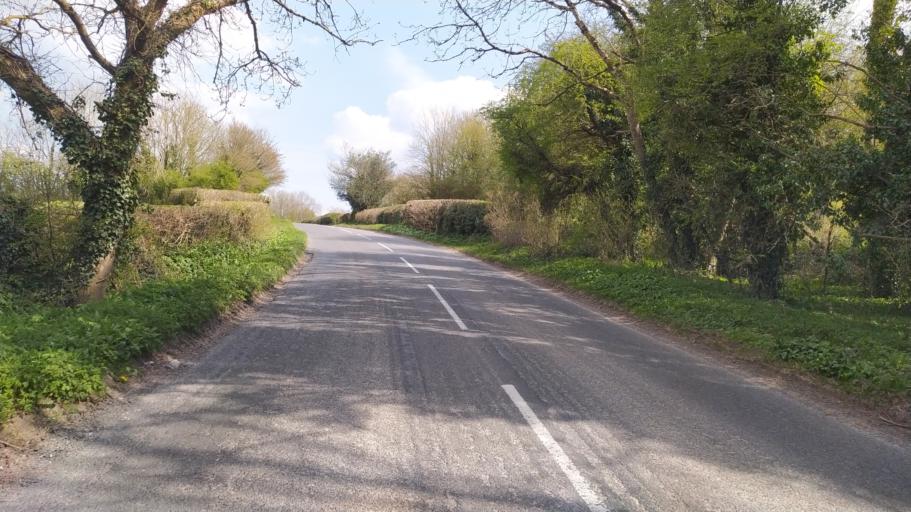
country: GB
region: England
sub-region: Somerset
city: Frome
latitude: 51.2364
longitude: -2.3899
